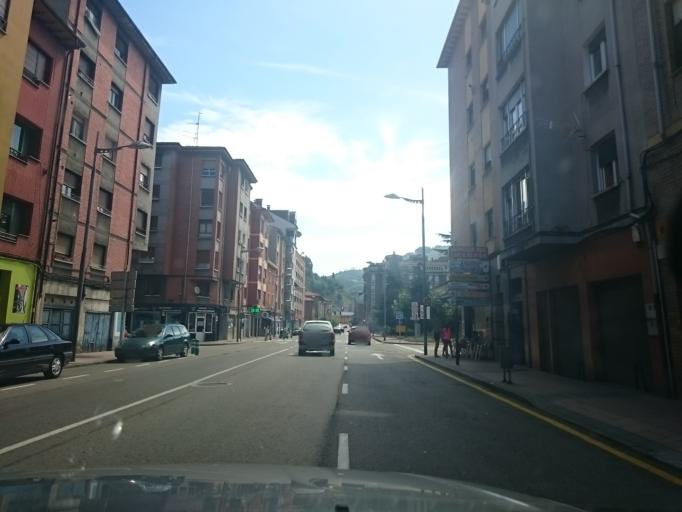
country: ES
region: Asturias
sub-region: Province of Asturias
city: Mieres
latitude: 43.2548
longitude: -5.7809
